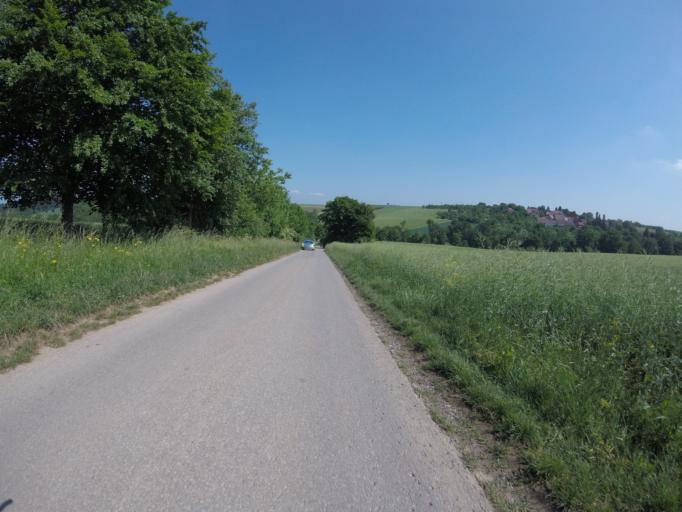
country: DE
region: Baden-Wuerttemberg
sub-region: Regierungsbezirk Stuttgart
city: Steinheim am der Murr
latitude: 48.9727
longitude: 9.3069
